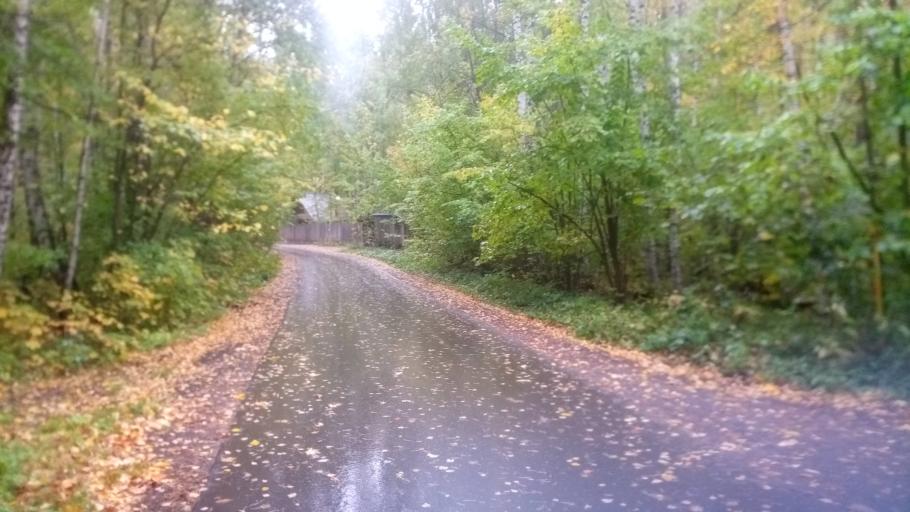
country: RU
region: Tatarstan
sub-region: Tukayevskiy Rayon
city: Naberezhnyye Chelny
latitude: 55.8514
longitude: 52.4619
